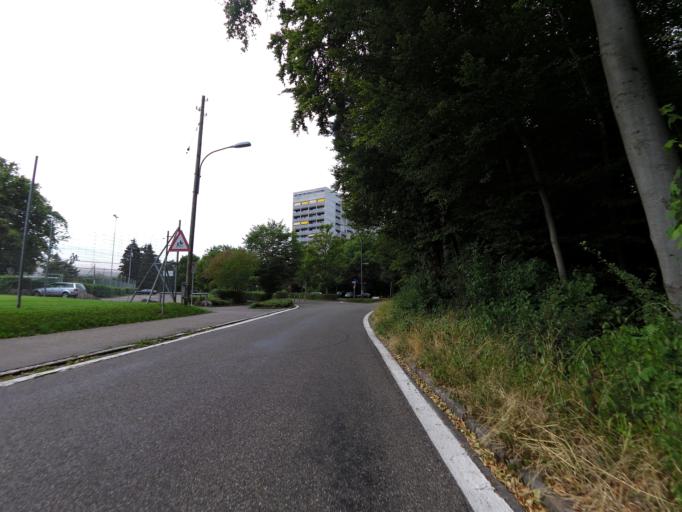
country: CH
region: Zurich
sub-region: Bezirk Zuerich
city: Zuerich (Kreis 11) / Affoltern
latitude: 47.4201
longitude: 8.5141
